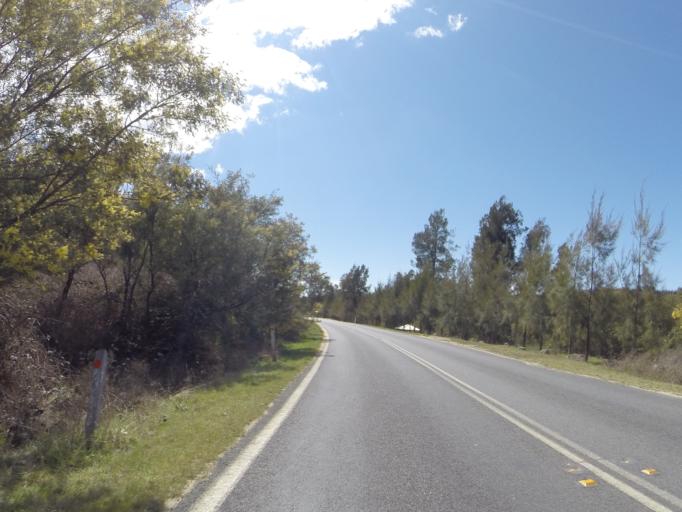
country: AU
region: Australian Capital Territory
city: Macquarie
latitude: -35.3653
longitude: 148.9519
